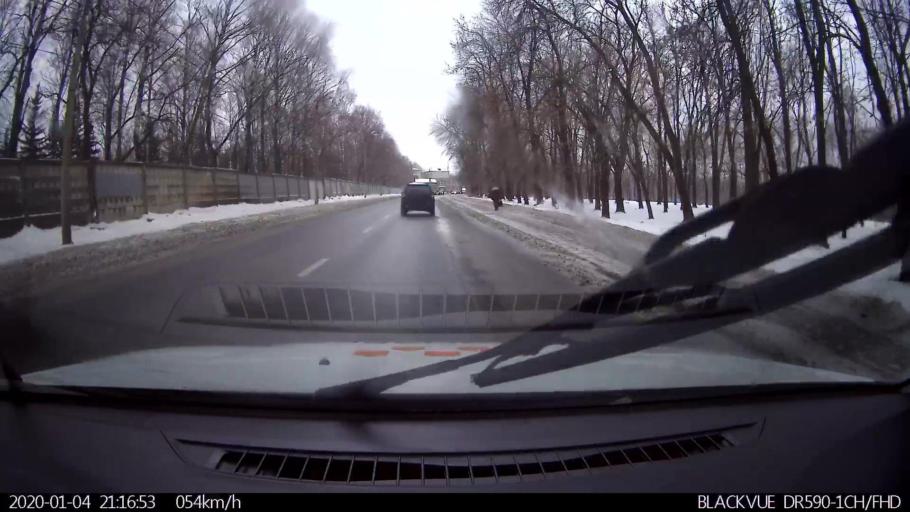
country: RU
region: Nizjnij Novgorod
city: Gorbatovka
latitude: 56.2378
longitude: 43.8506
